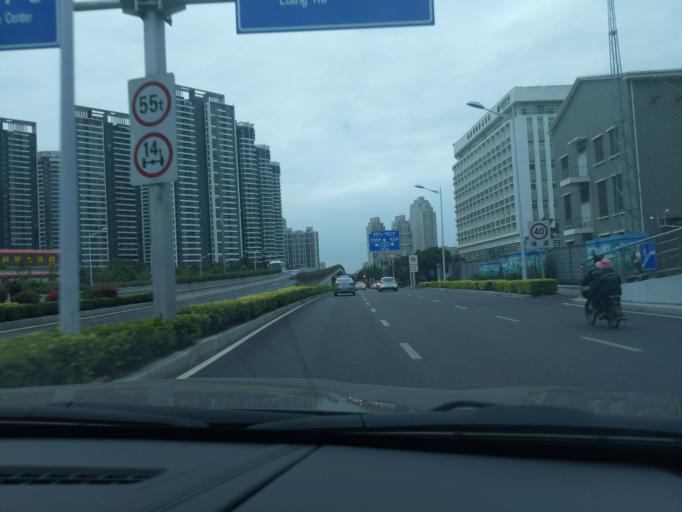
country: CN
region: Fujian
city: Liuwudian
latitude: 24.4846
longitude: 118.1822
